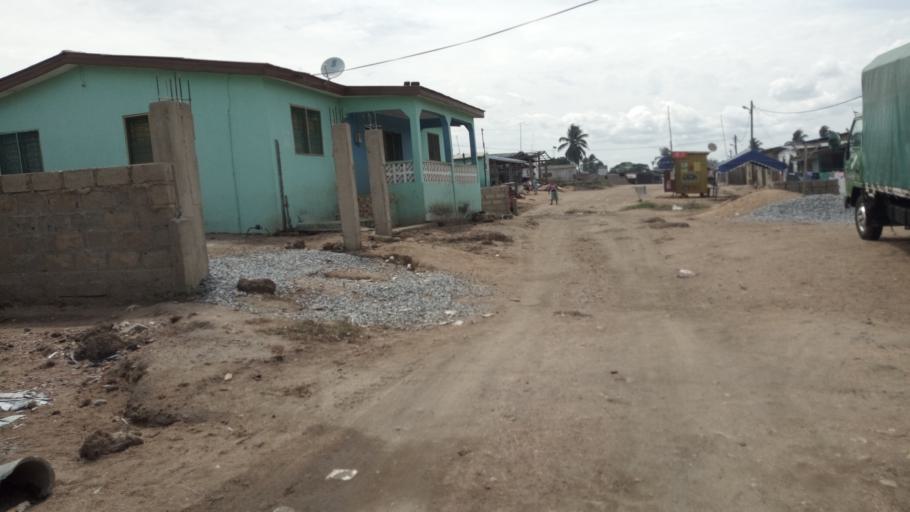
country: GH
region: Central
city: Winneba
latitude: 5.3477
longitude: -0.6154
